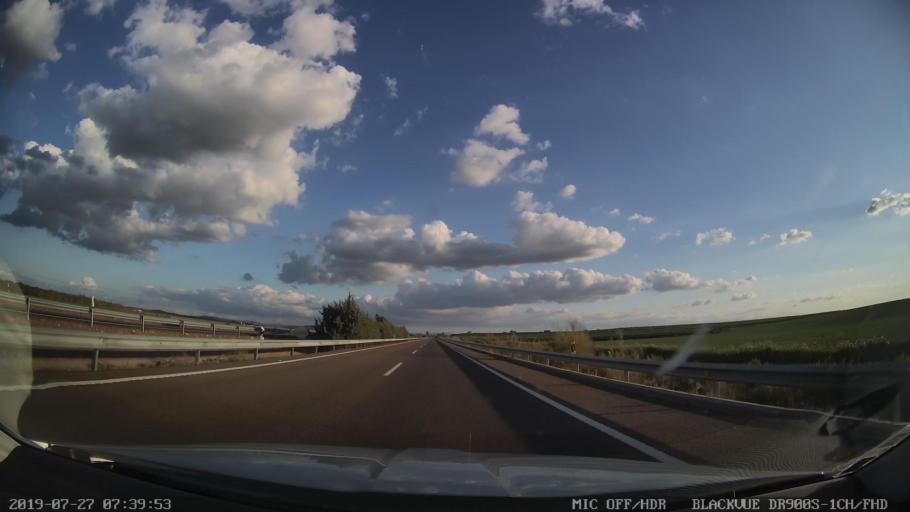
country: ES
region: Extremadura
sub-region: Provincia de Badajoz
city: Santa Amalia
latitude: 39.0564
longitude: -6.0571
